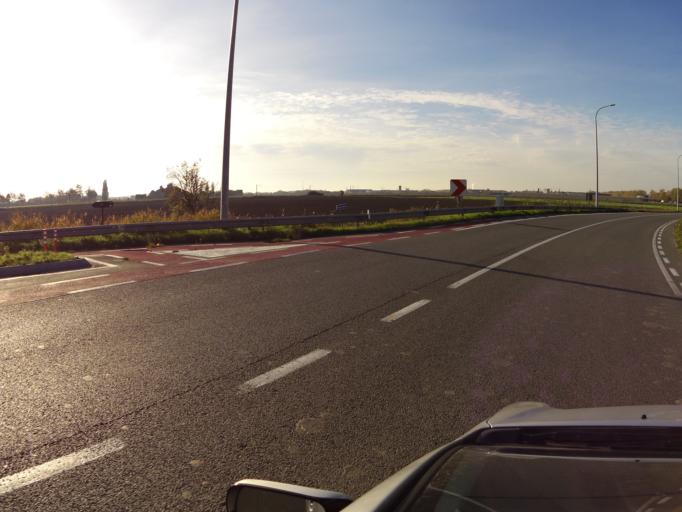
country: BE
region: Flanders
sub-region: Provincie West-Vlaanderen
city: Veurne
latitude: 51.0696
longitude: 2.7115
